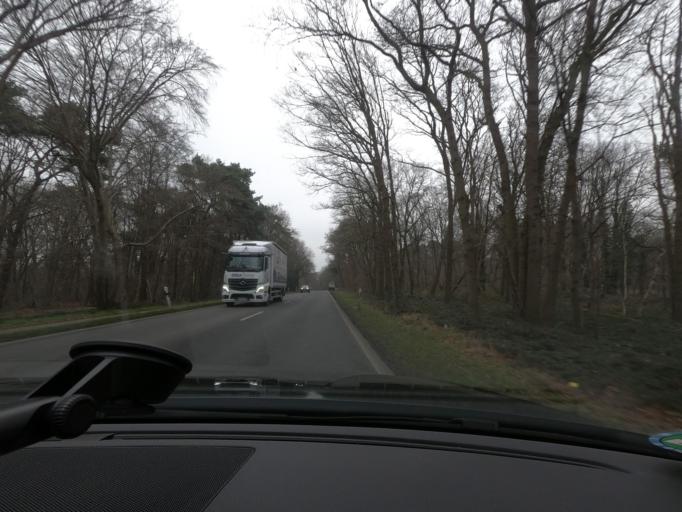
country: DE
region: North Rhine-Westphalia
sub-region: Regierungsbezirk Dusseldorf
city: Nettetal
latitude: 51.3475
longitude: 6.2323
